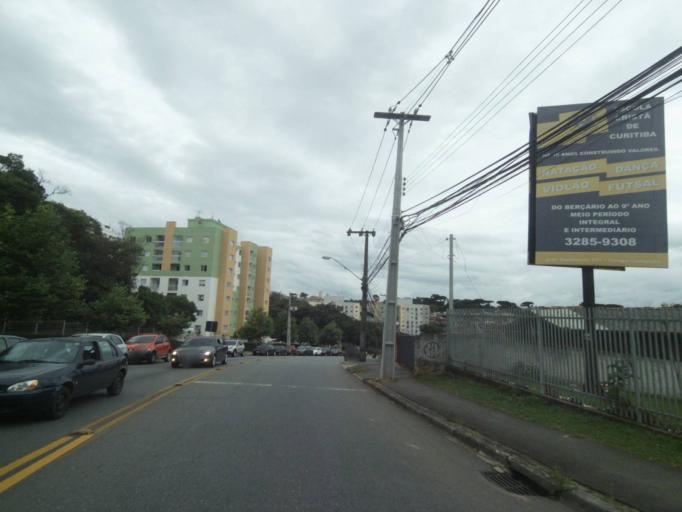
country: BR
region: Parana
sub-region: Curitiba
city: Curitiba
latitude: -25.4608
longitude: -49.3376
